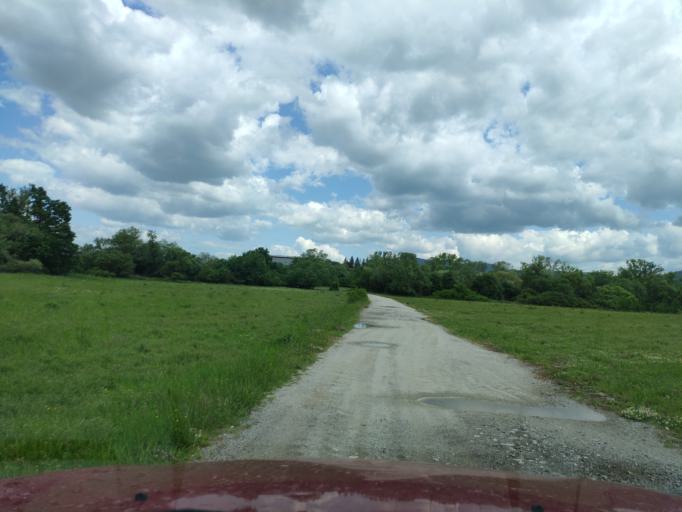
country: SK
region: Kosicky
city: Kosice
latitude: 48.8404
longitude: 21.3207
